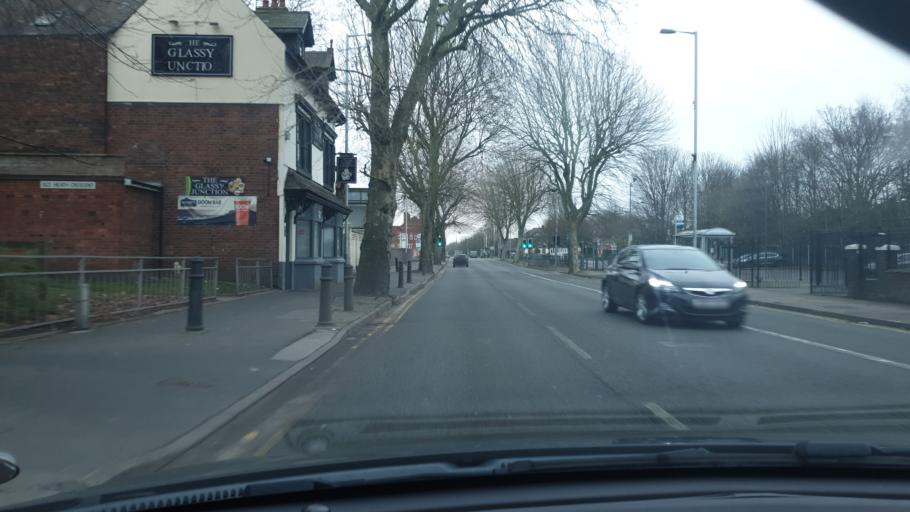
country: GB
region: England
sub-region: Wolverhampton
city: Wednesfield
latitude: 52.5834
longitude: -2.1017
